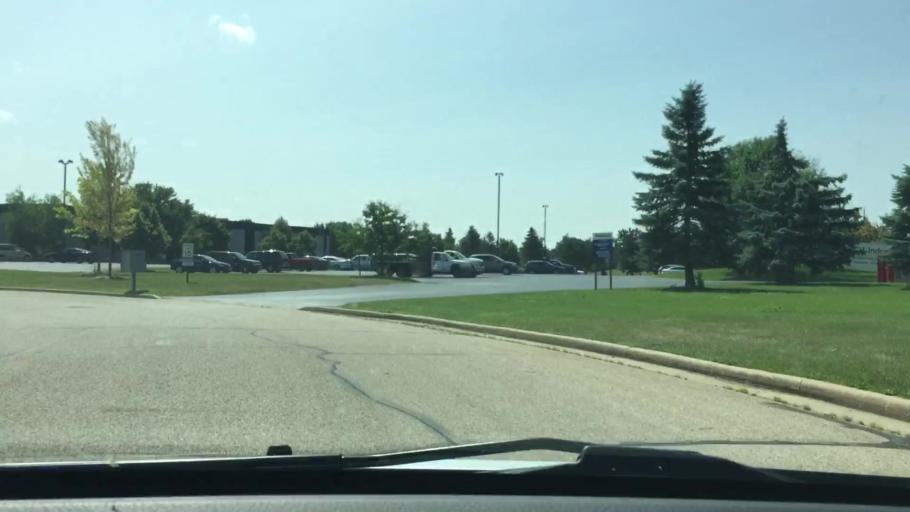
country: US
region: Wisconsin
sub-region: Waukesha County
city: Oconomowoc
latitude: 43.0738
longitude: -88.4785
